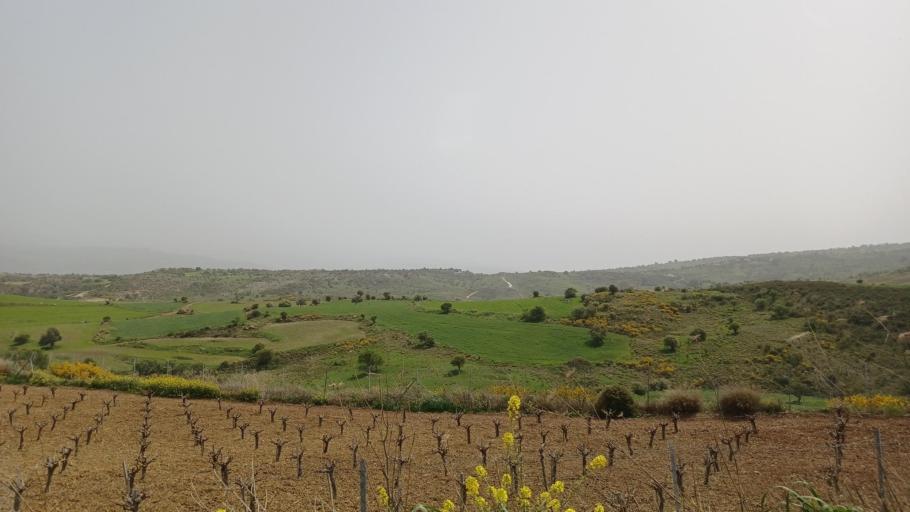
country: CY
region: Pafos
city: Polis
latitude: 34.9882
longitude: 32.3887
